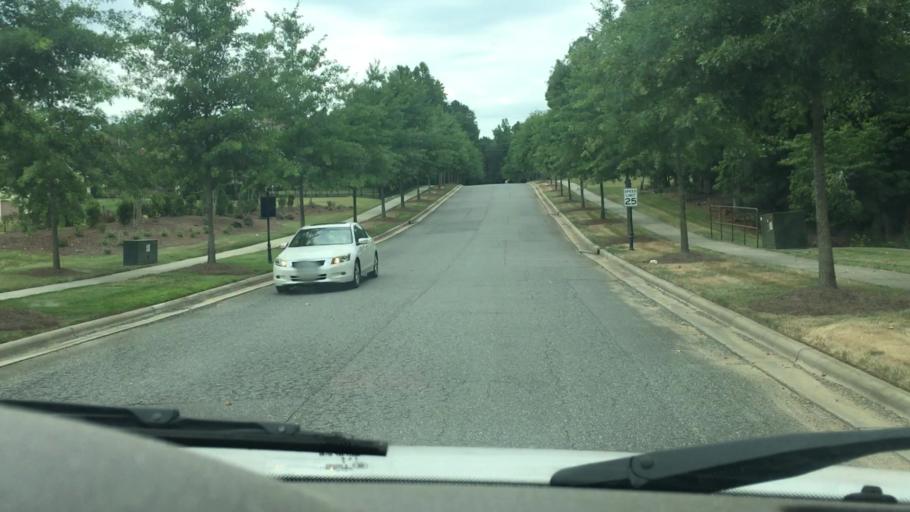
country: US
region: North Carolina
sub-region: Gaston County
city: Davidson
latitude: 35.4611
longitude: -80.7795
